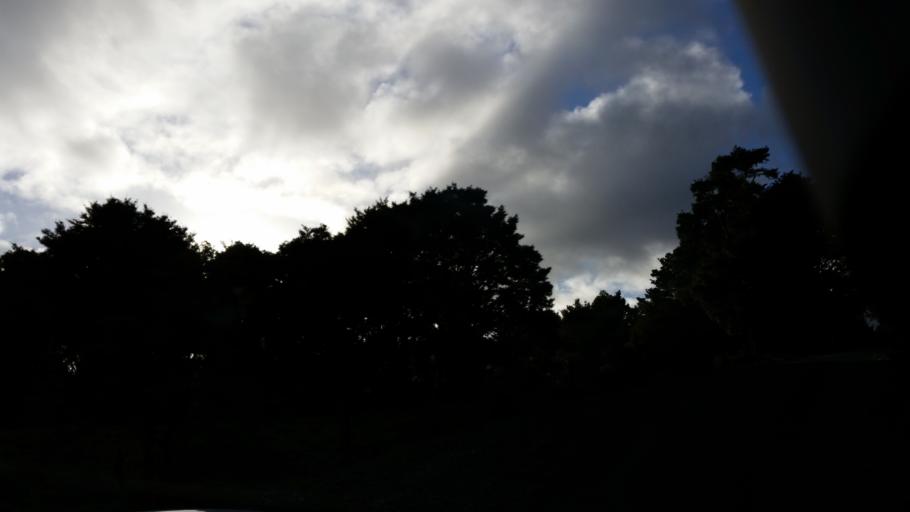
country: NZ
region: Northland
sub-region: Whangarei
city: Maungatapere
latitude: -35.7783
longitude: 174.0973
